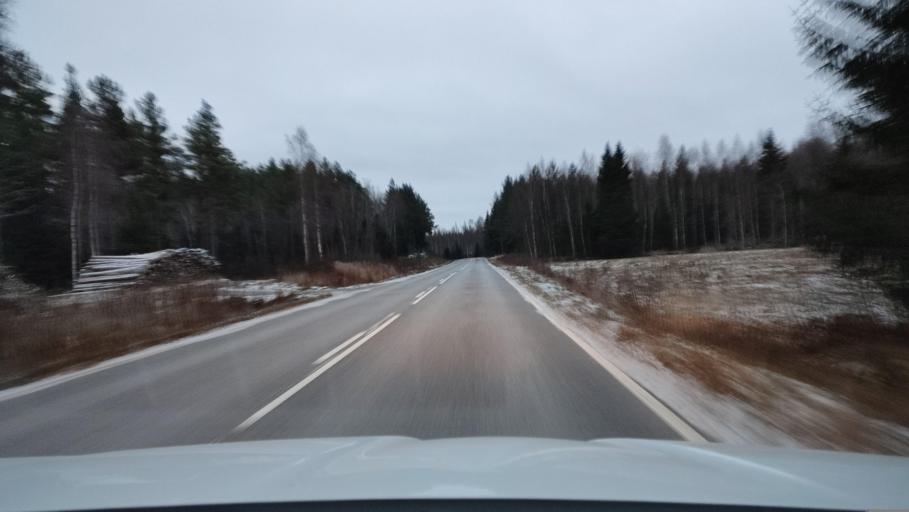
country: FI
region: Ostrobothnia
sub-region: Vaasa
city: Replot
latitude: 63.2414
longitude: 21.3842
